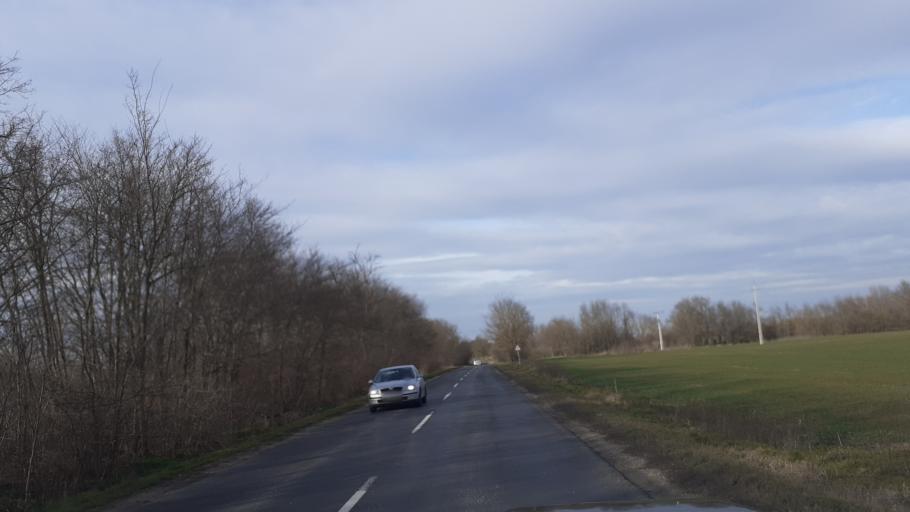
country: HU
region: Fejer
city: Kaloz
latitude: 46.9706
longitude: 18.4815
